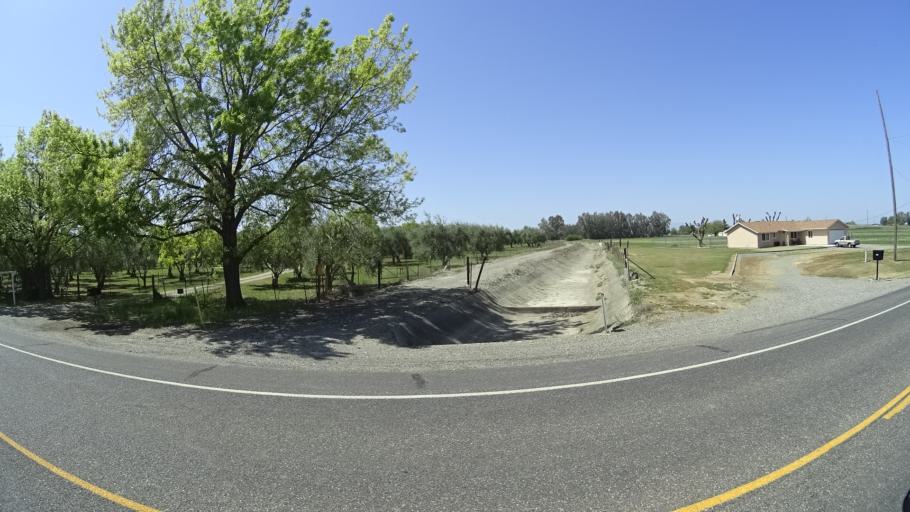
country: US
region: California
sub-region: Glenn County
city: Orland
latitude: 39.7906
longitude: -122.1975
